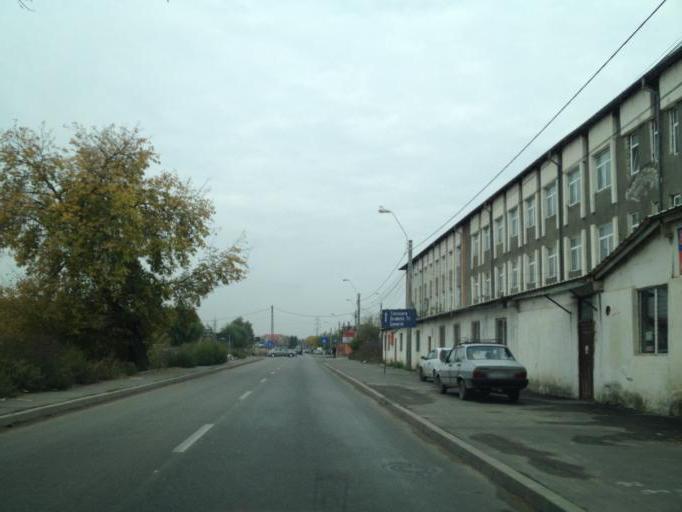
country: RO
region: Dolj
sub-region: Municipiul Craiova
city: Popoveni
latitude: 44.2938
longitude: 23.7901
